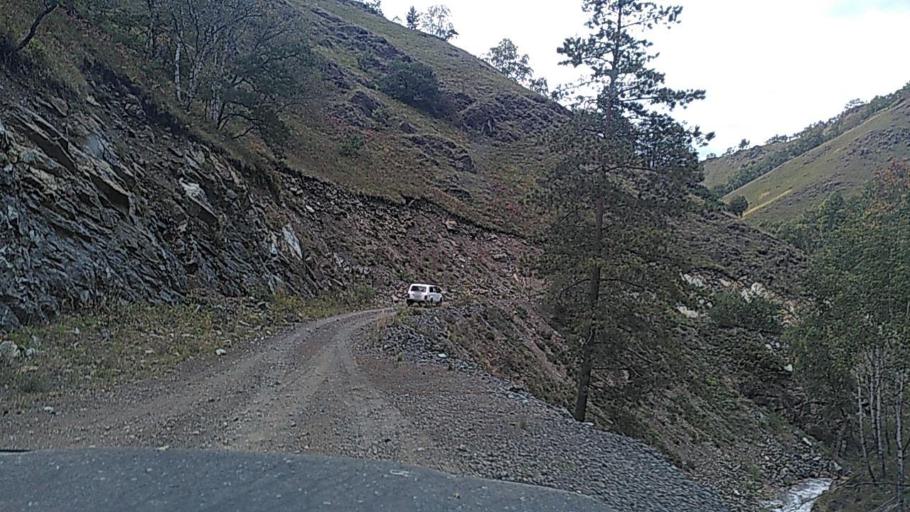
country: RU
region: Kabardino-Balkariya
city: Kamennomostskoye
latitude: 43.7128
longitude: 42.8461
